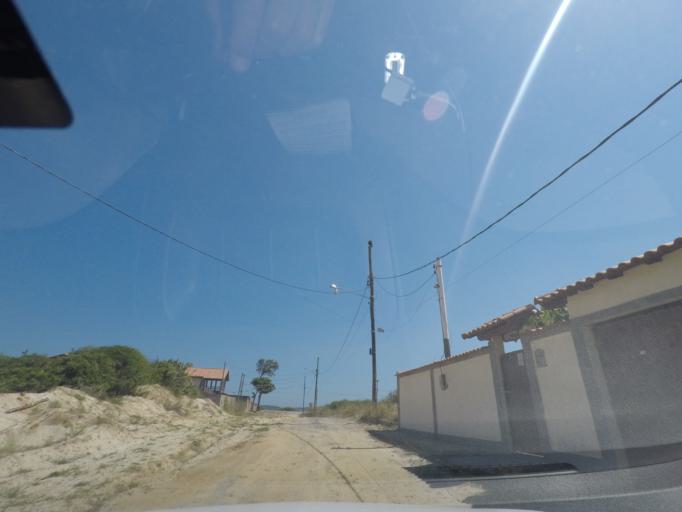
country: BR
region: Rio de Janeiro
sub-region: Marica
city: Marica
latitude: -22.9732
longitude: -42.9172
